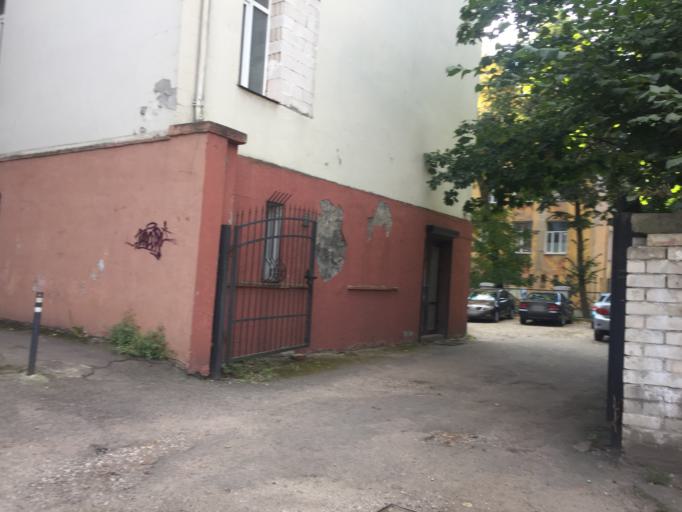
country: RU
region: Kaliningrad
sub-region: Gorod Kaliningrad
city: Kaliningrad
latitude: 54.6977
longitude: 20.5088
